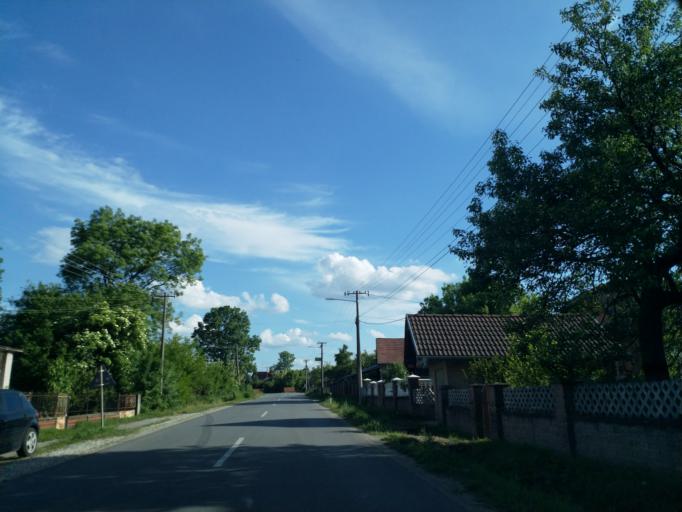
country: RS
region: Central Serbia
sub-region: Sumadijski Okrug
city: Lapovo
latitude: 44.1890
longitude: 21.0909
